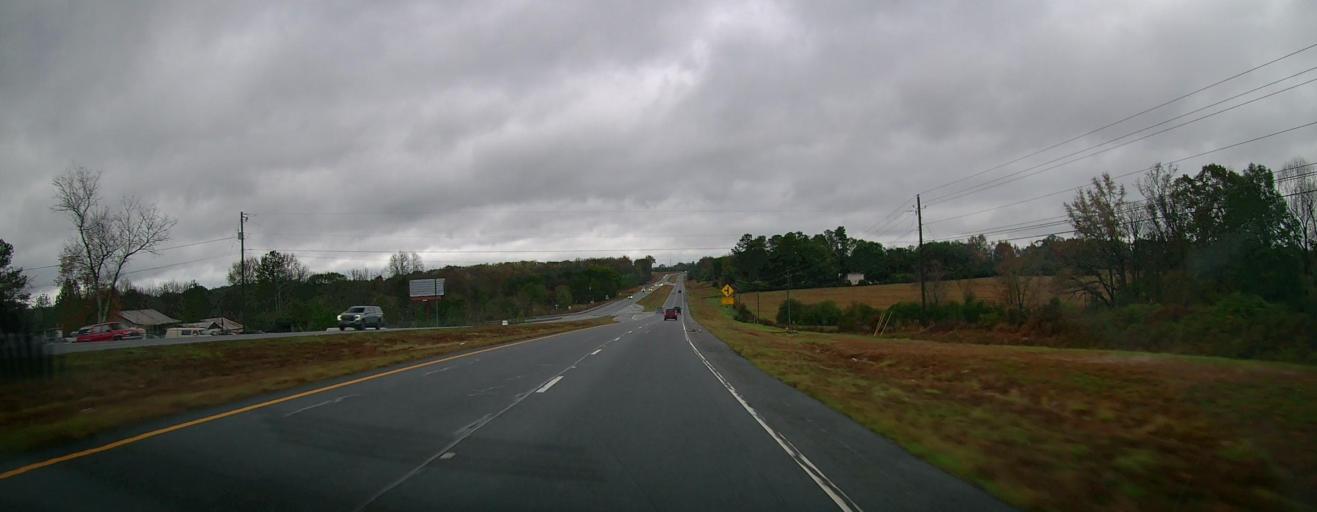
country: US
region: Georgia
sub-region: Jackson County
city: Nicholson
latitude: 34.1564
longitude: -83.4433
